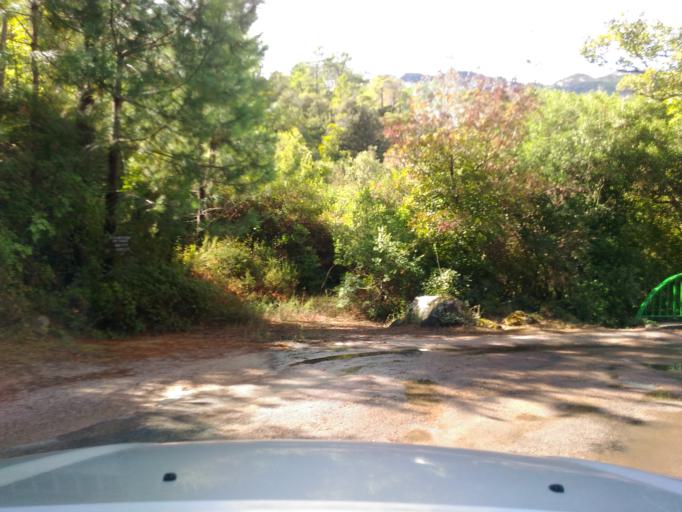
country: FR
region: Corsica
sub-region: Departement de la Corse-du-Sud
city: Porto-Vecchio
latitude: 41.7135
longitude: 9.3033
